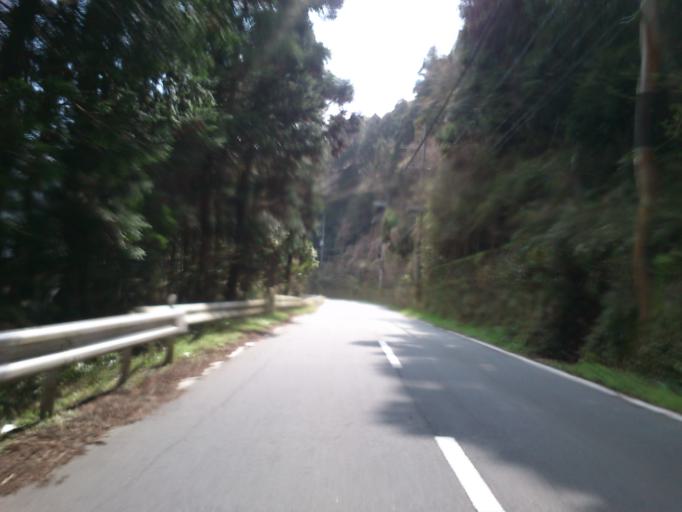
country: JP
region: Mie
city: Ueno-ebisumachi
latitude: 34.7653
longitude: 135.9928
